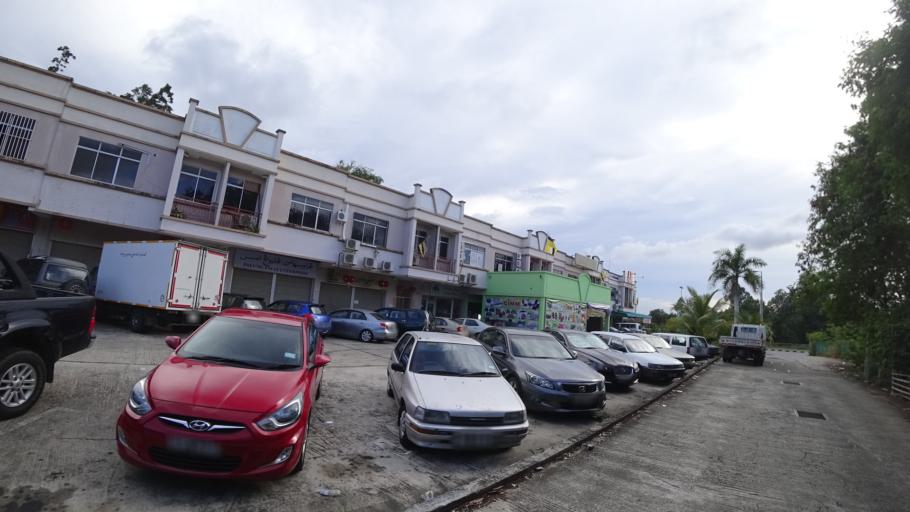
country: BN
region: Brunei and Muara
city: Bandar Seri Begawan
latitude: 4.8716
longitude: 114.8629
